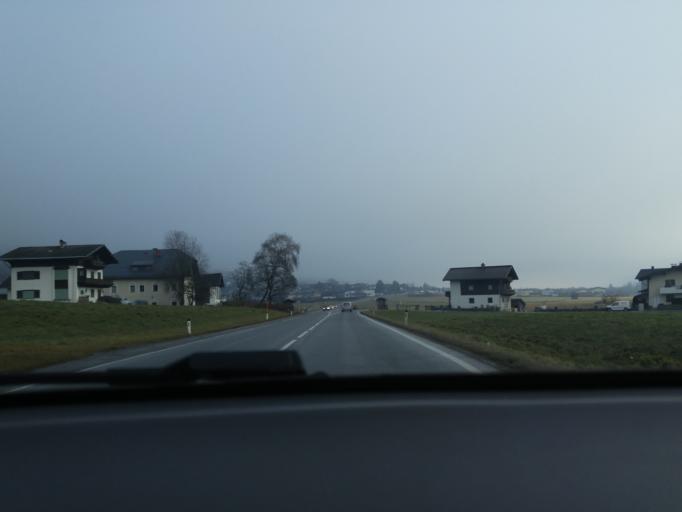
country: AT
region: Salzburg
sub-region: Politischer Bezirk Zell am See
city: Niedernsill
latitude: 47.2834
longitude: 12.6316
